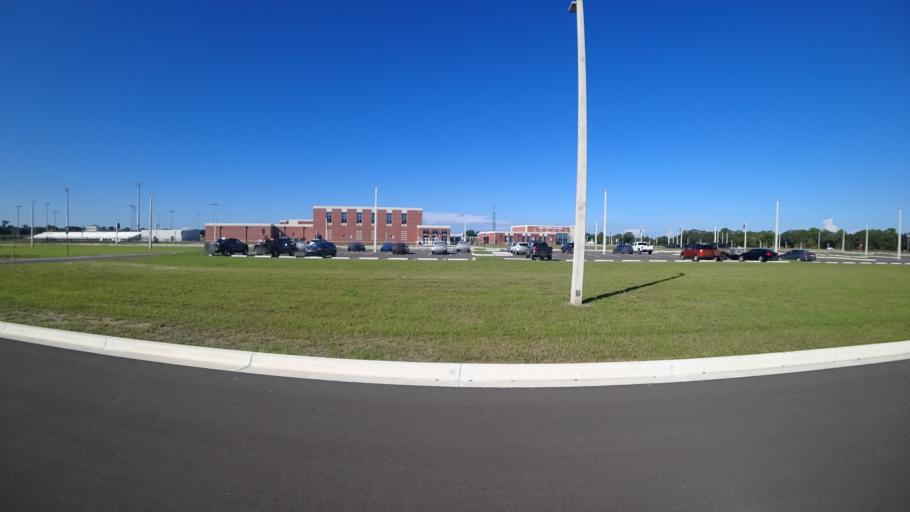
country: US
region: Florida
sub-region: Manatee County
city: Ellenton
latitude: 27.5816
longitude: -82.4374
